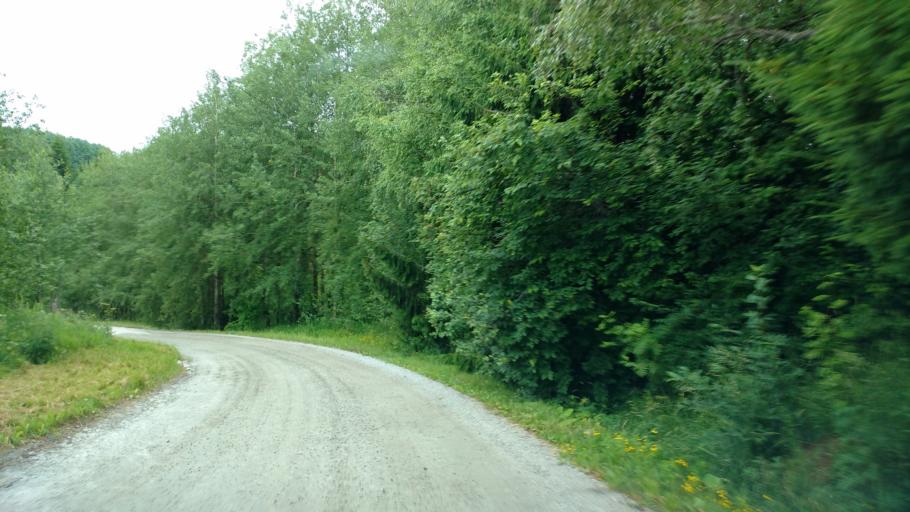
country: FI
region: Varsinais-Suomi
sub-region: Salo
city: Halikko
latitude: 60.4782
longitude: 23.0019
